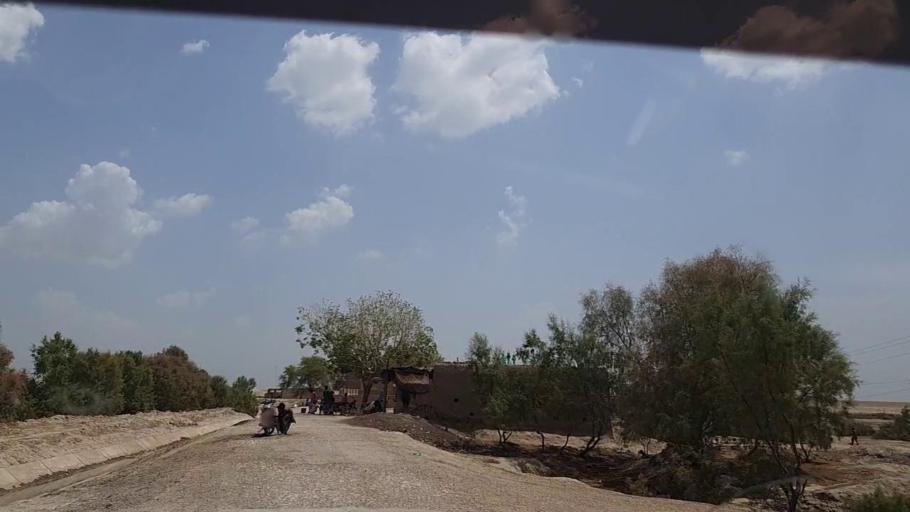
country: PK
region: Sindh
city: Bhan
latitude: 26.5053
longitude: 67.6393
